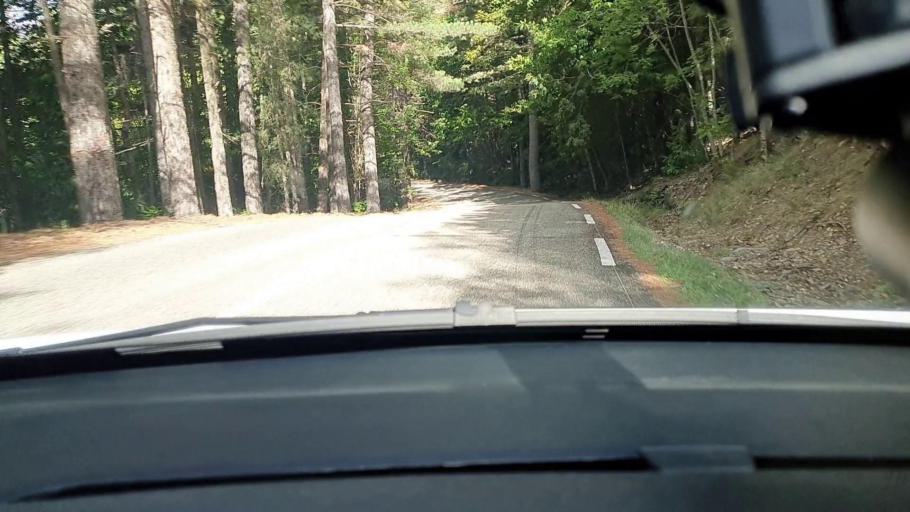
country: FR
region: Rhone-Alpes
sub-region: Departement de l'Ardeche
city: Les Vans
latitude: 44.4209
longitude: 3.9712
